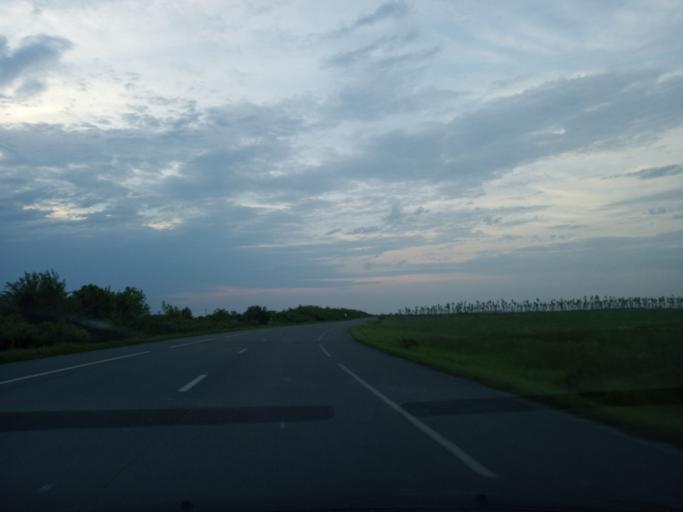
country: RO
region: Timis
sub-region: Oras Deta
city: Deta
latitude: 45.4093
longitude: 21.2302
